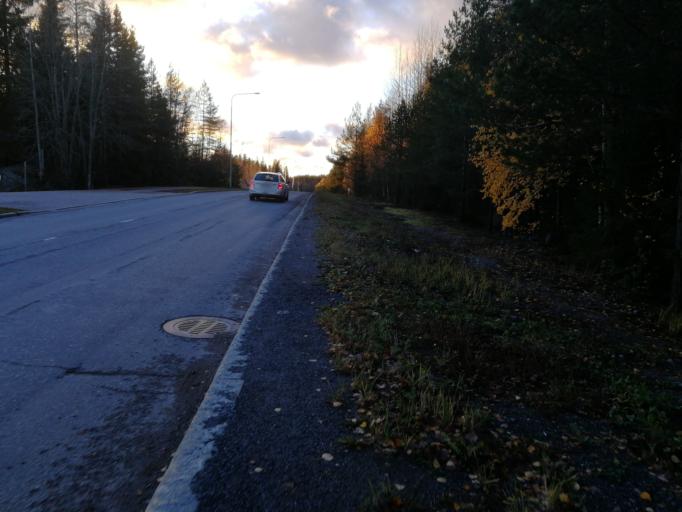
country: FI
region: Pirkanmaa
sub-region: Tampere
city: Tampere
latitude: 61.4531
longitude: 23.9005
